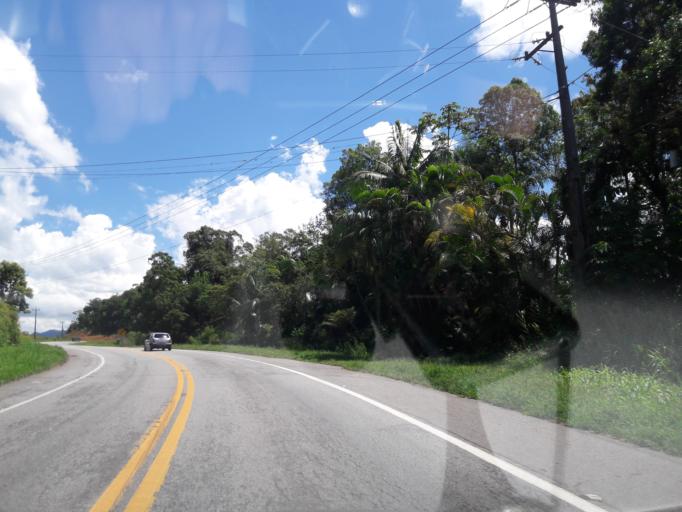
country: BR
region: Parana
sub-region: Antonina
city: Antonina
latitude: -25.4566
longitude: -48.8126
